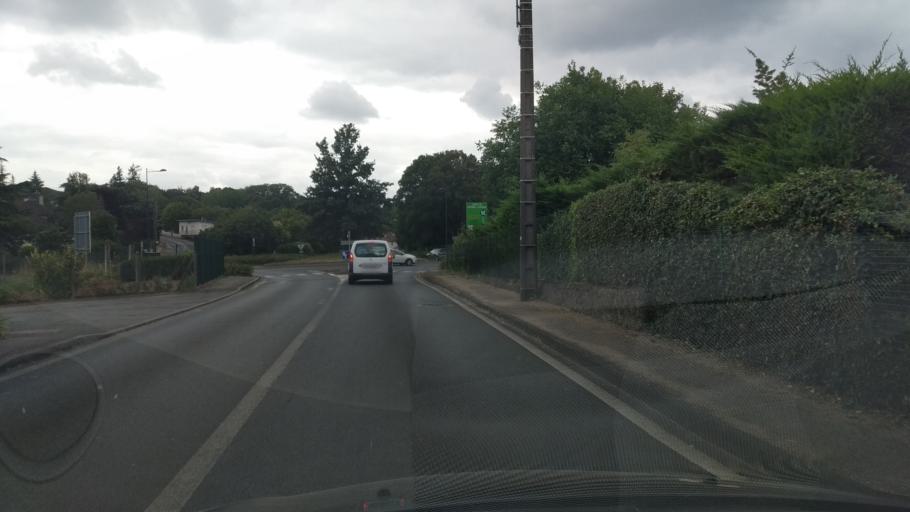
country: FR
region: Poitou-Charentes
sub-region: Departement de la Vienne
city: Saint-Benoit
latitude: 46.5597
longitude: 0.3553
